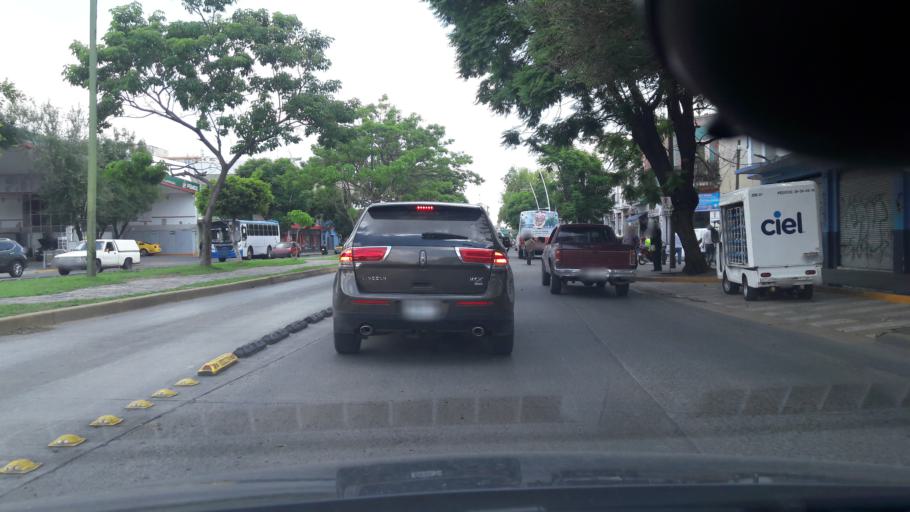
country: MX
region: Jalisco
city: Guadalajara
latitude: 20.6675
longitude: -103.3459
